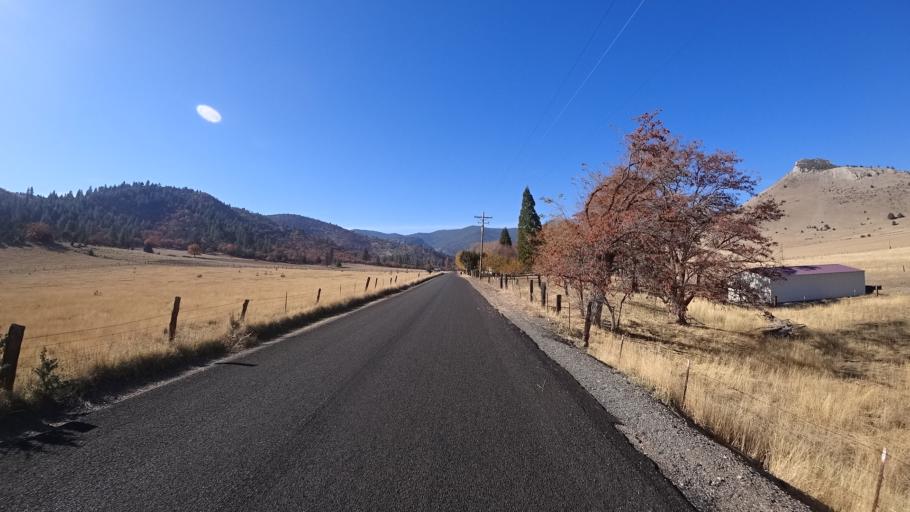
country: US
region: California
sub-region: Siskiyou County
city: Weed
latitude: 41.5030
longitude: -122.5618
